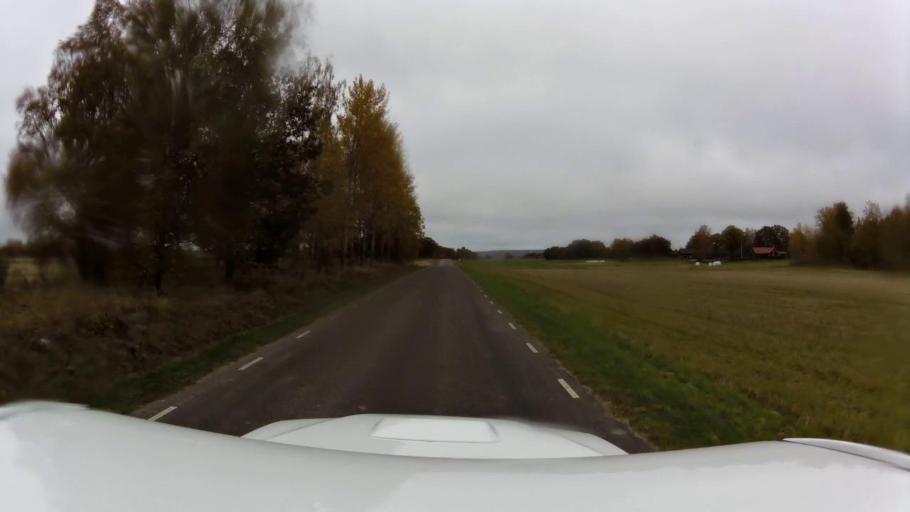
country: SE
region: OEstergoetland
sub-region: Linkopings Kommun
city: Linghem
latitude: 58.4717
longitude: 15.7626
